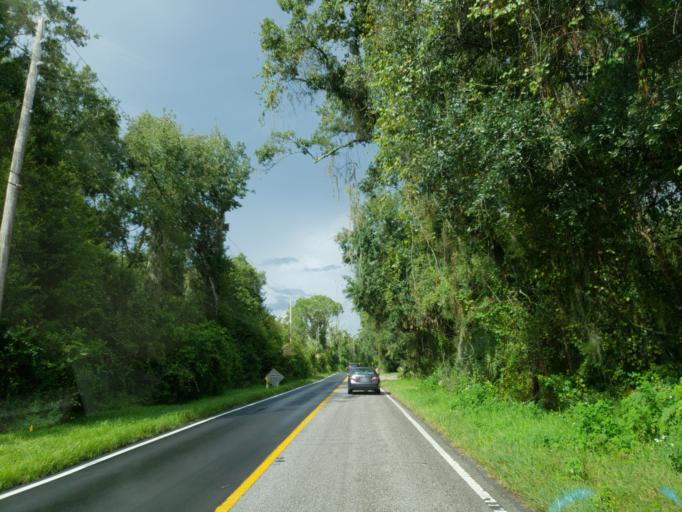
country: US
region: Florida
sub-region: Pasco County
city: Land O' Lakes
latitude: 28.2472
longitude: -82.4524
